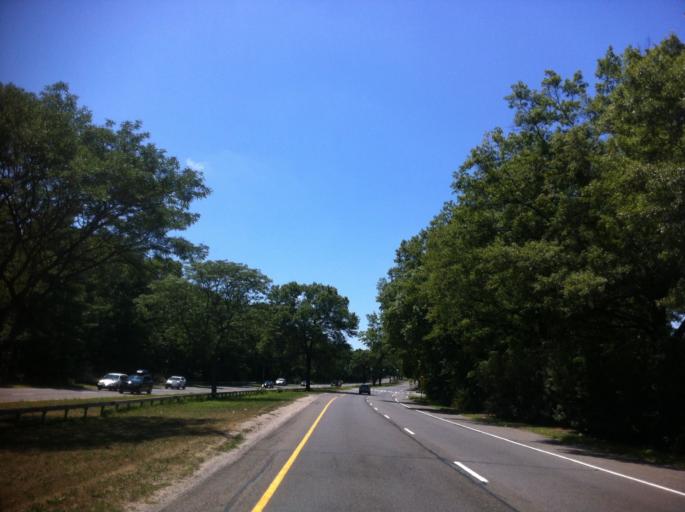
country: US
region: New York
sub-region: Nassau County
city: Glen Head
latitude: 40.8345
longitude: -73.6181
